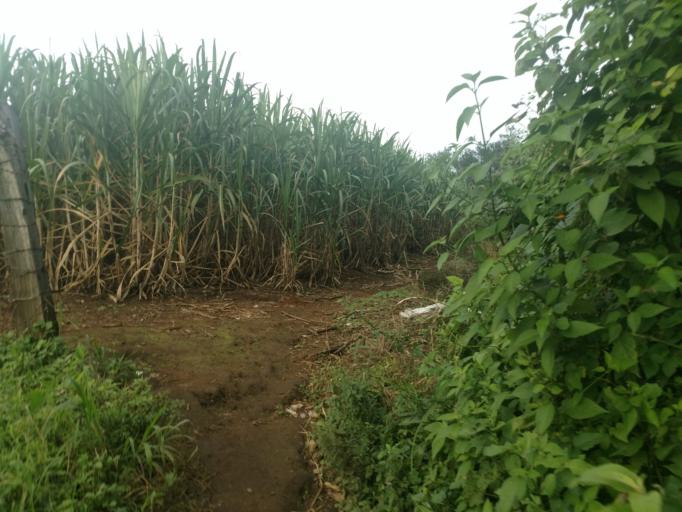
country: MX
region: Nayarit
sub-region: Tepic
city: La Corregidora
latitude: 21.4641
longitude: -104.8049
